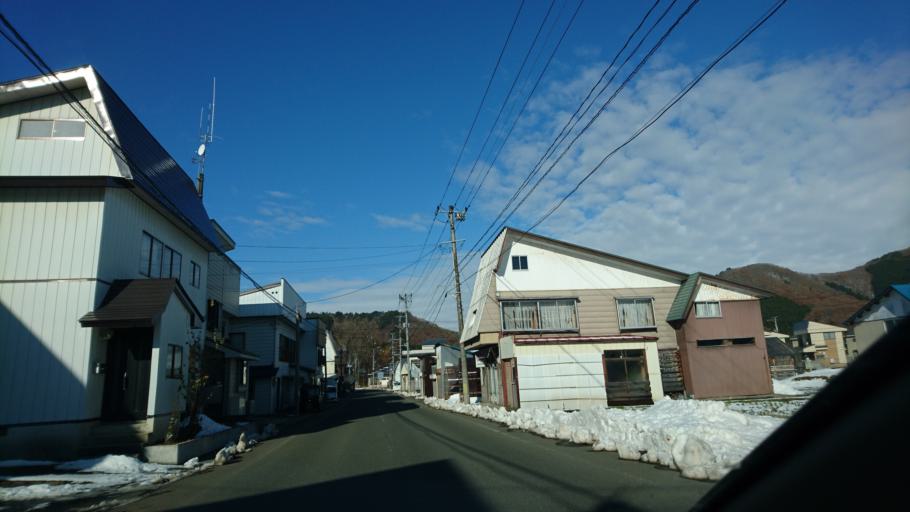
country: JP
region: Akita
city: Yokotemachi
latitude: 39.3115
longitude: 140.7780
